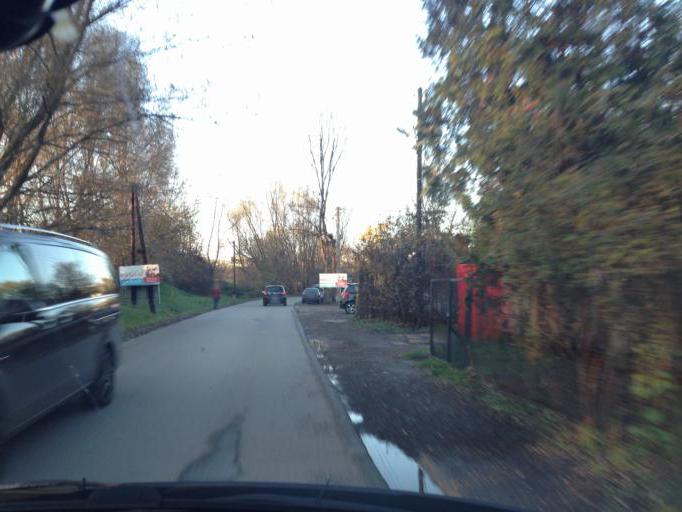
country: PL
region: Lesser Poland Voivodeship
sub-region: Powiat krakowski
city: Rzaska
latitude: 50.0740
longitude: 19.8776
